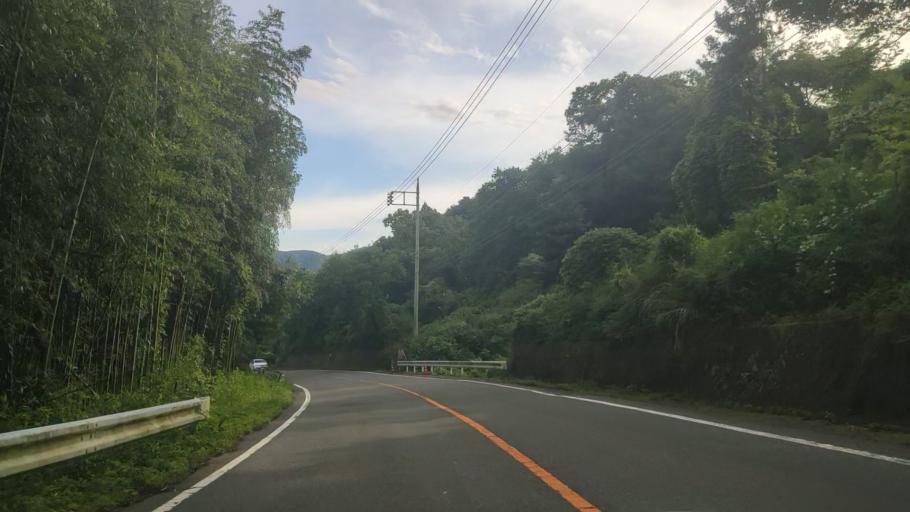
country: JP
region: Gunma
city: Omamacho-omama
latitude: 36.5193
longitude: 139.3033
